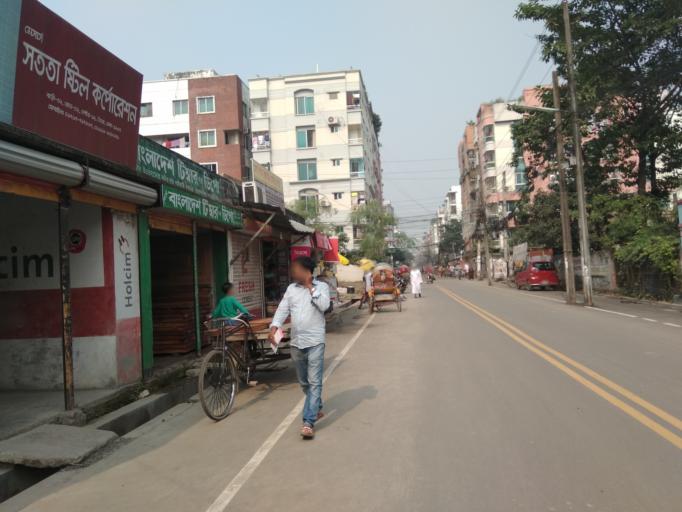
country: BD
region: Dhaka
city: Tungi
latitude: 23.8687
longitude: 90.3833
